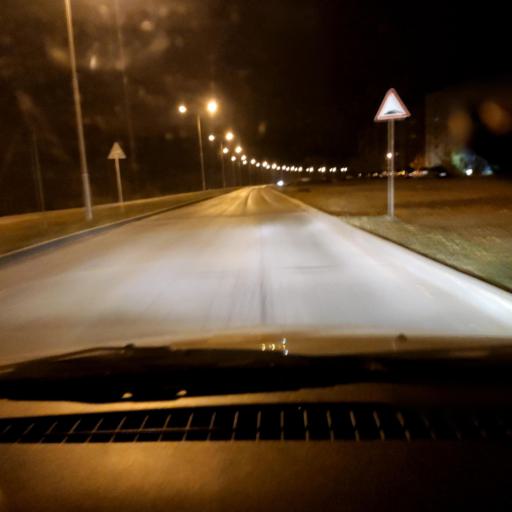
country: RU
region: Bashkortostan
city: Ufa
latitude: 54.7731
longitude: 56.0851
